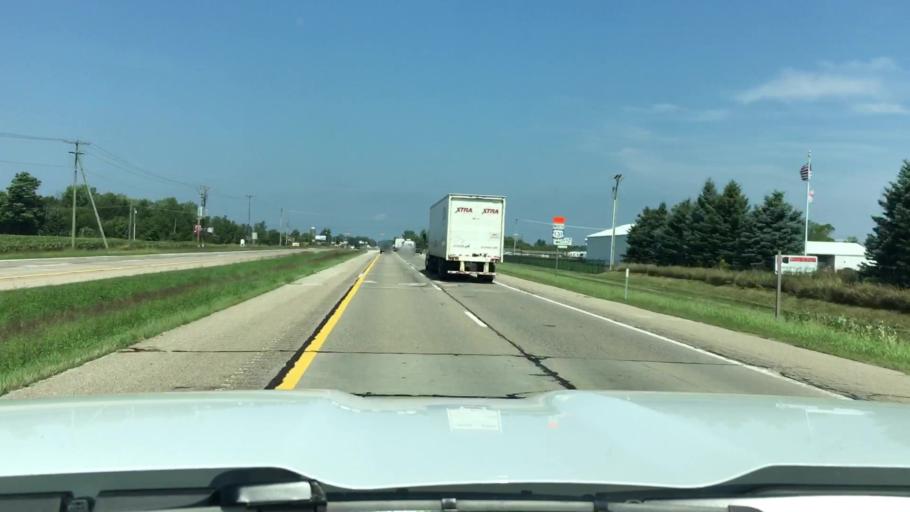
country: US
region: Michigan
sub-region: Kalamazoo County
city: Schoolcraft
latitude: 42.0895
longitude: -85.6367
